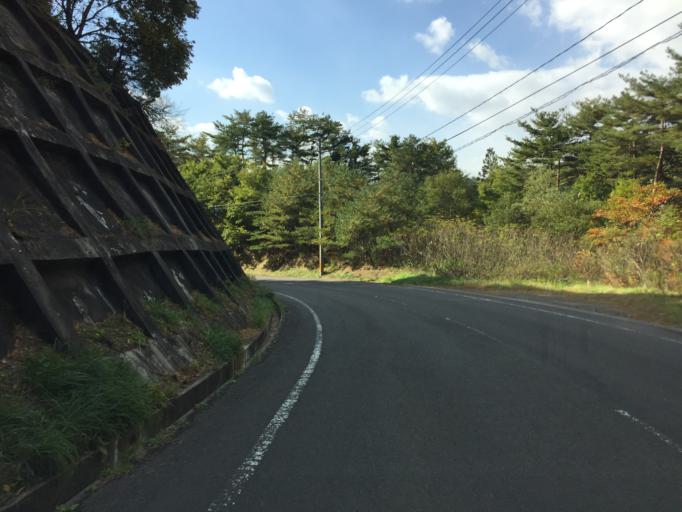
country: JP
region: Fukushima
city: Fukushima-shi
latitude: 37.8075
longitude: 140.3890
